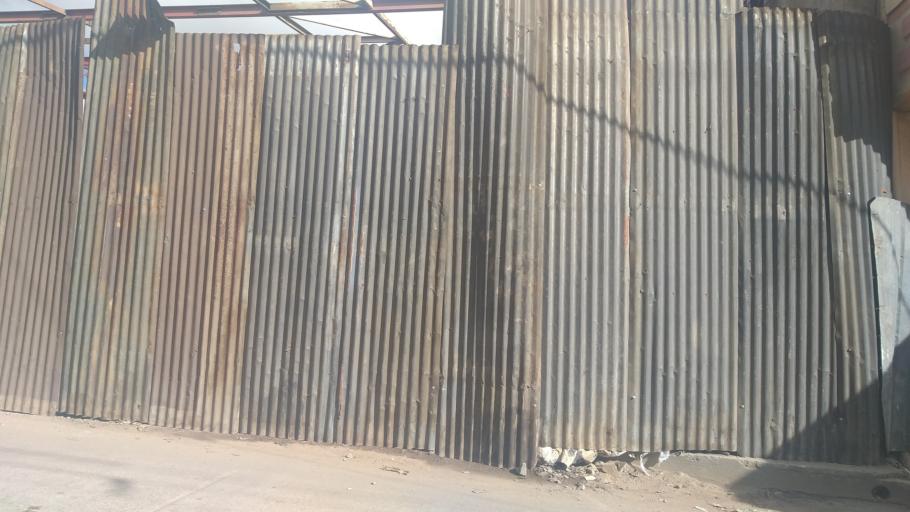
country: GT
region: Quetzaltenango
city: Ostuncalco
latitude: 14.8684
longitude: -91.6239
